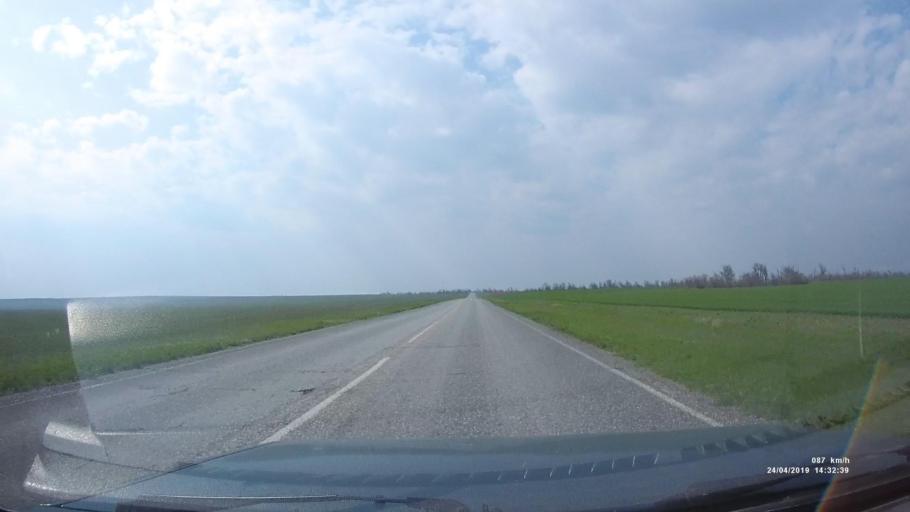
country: RU
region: Kalmykiya
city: Arshan'
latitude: 46.3664
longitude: 43.9657
